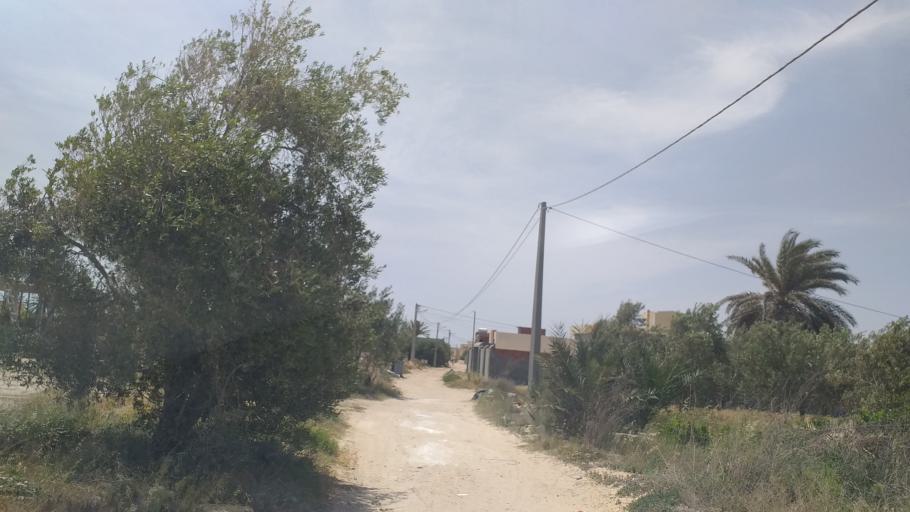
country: TN
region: Qabis
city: Gabes
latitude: 33.9535
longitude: 10.0632
